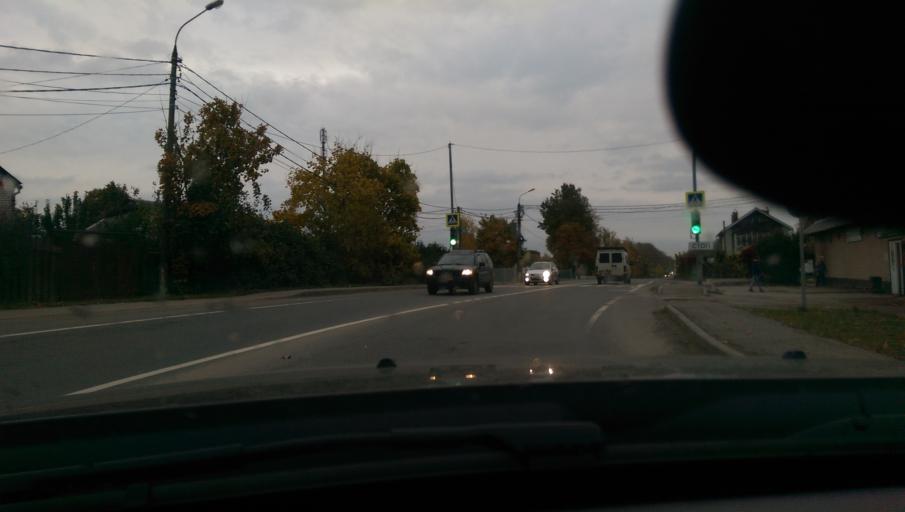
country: RU
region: Moskovskaya
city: Pirogovskiy
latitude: 55.9684
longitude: 37.6765
